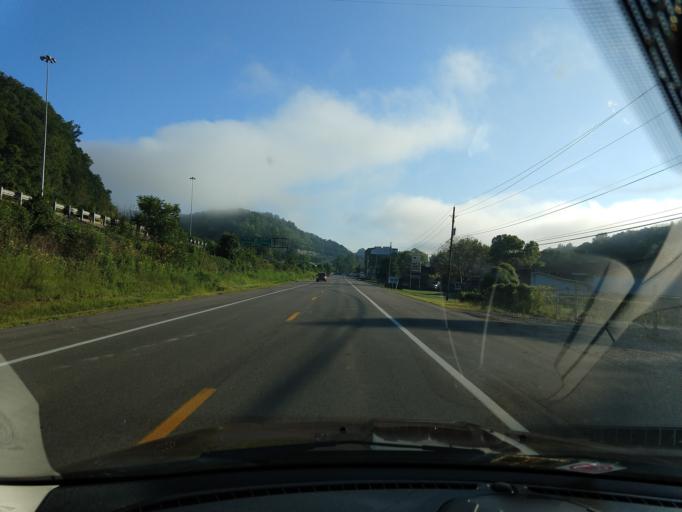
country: US
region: West Virginia
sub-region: Kanawha County
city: Charleston
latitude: 38.3757
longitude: -81.6043
